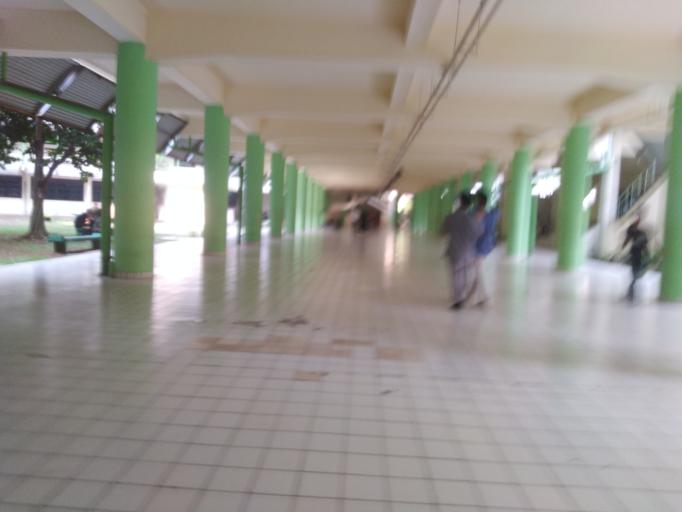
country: ID
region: West Java
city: Ciampea
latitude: -6.5591
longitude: 106.7301
